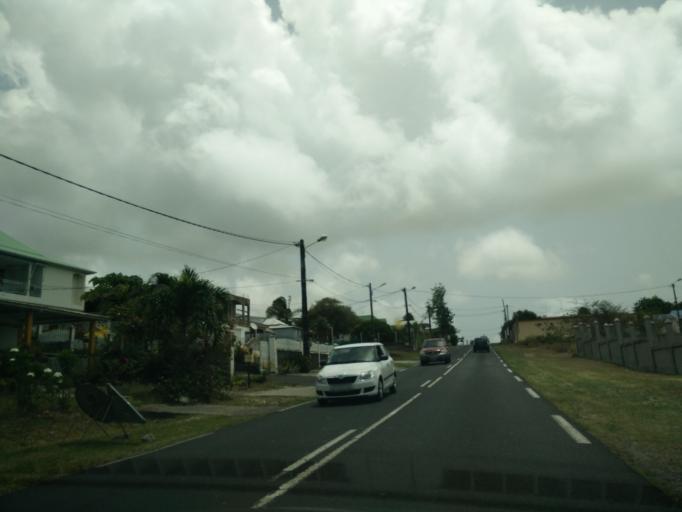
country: GP
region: Guadeloupe
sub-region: Guadeloupe
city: Petit-Canal
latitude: 16.3587
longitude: -61.4558
